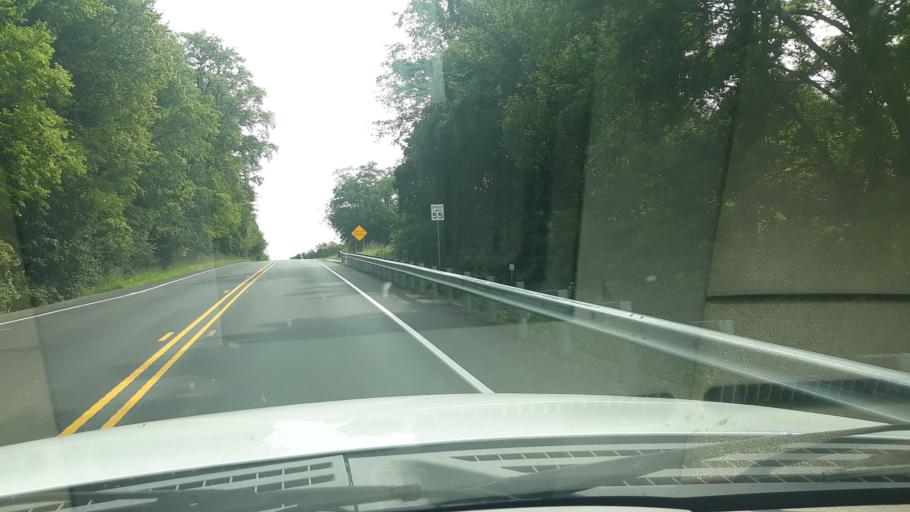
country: US
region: Indiana
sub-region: Gibson County
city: Owensville
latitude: 38.3558
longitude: -87.6591
